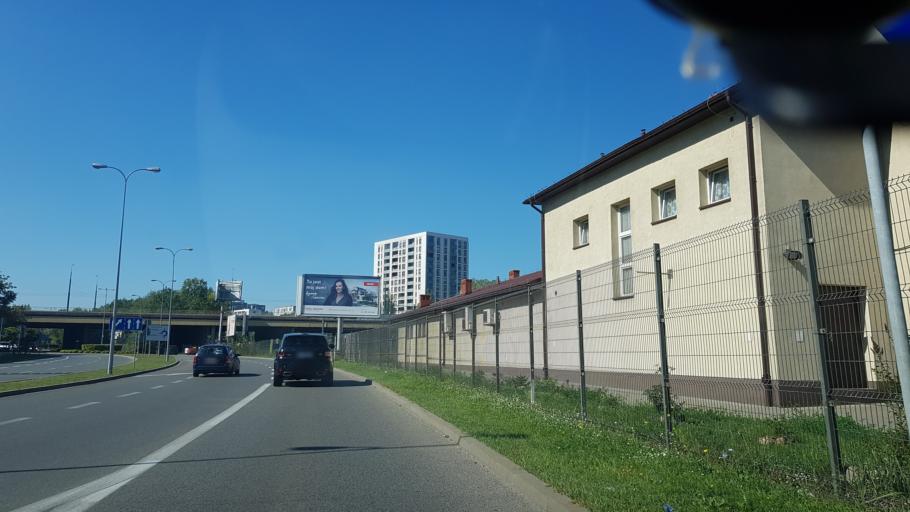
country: PL
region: Masovian Voivodeship
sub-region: Warszawa
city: Zoliborz
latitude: 52.2590
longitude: 20.9841
